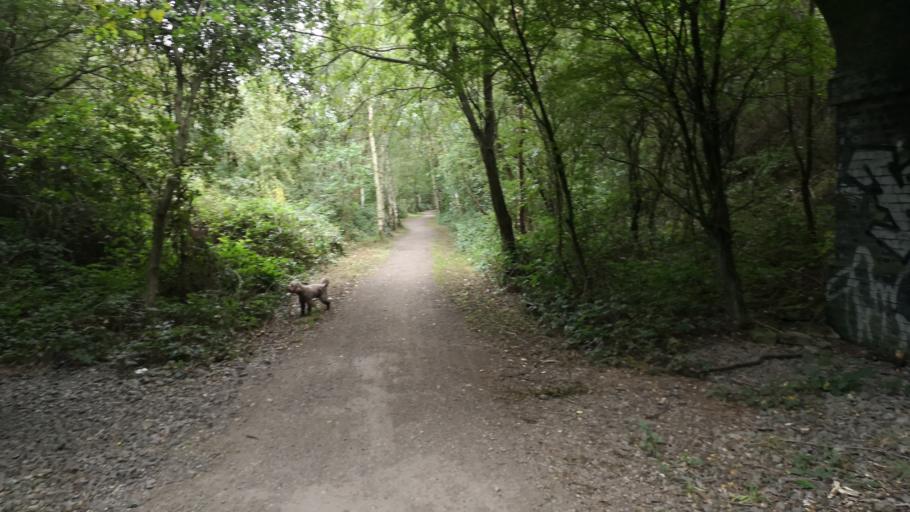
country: GB
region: England
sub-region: Barnsley
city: Royston
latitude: 53.6182
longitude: -1.4549
